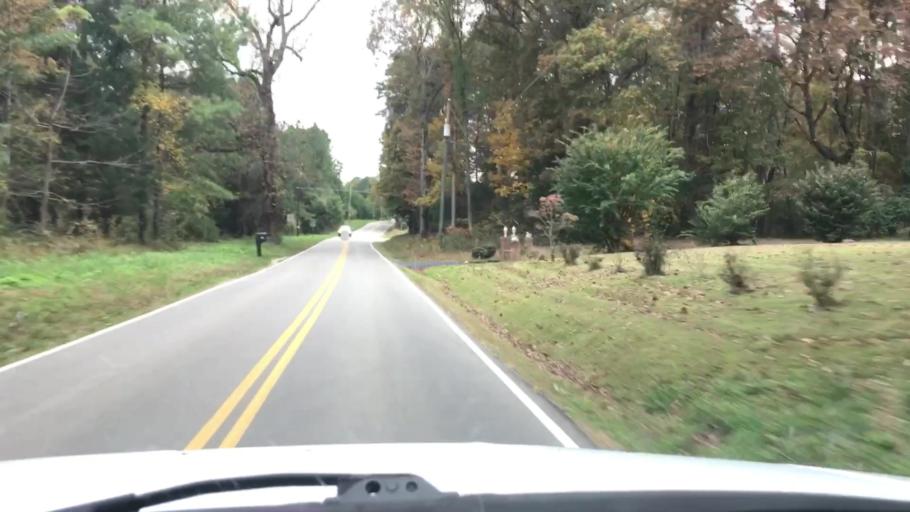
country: US
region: Virginia
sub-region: Goochland County
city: Goochland
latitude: 37.6803
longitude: -77.8714
